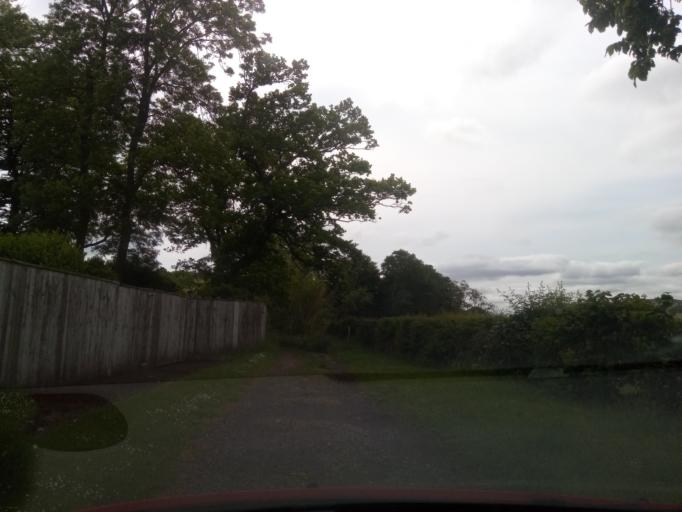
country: GB
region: Scotland
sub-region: The Scottish Borders
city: Selkirk
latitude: 55.5641
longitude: -2.8128
